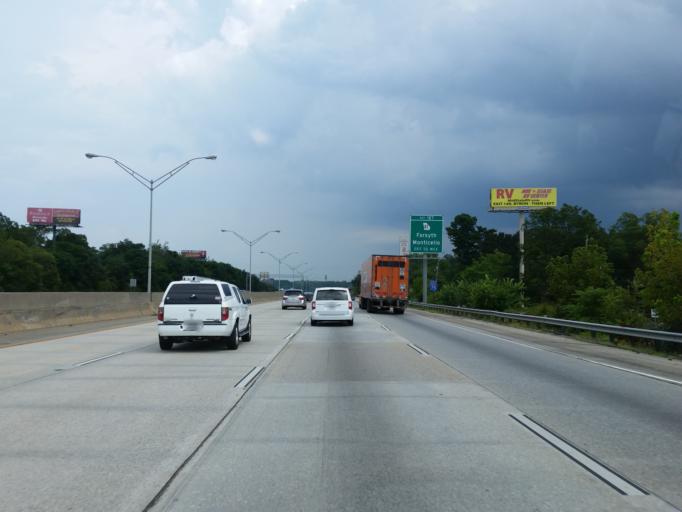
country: US
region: Georgia
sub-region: Monroe County
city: Forsyth
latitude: 33.0492
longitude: -83.9462
